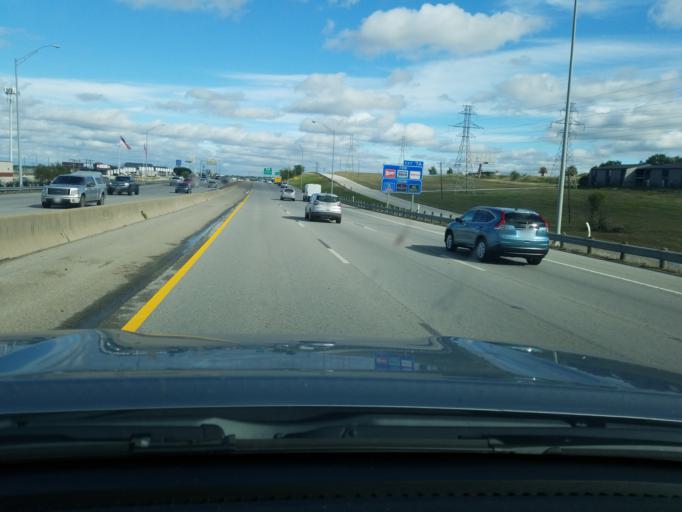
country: US
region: Texas
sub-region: Tarrant County
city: White Settlement
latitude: 32.7381
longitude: -97.4588
